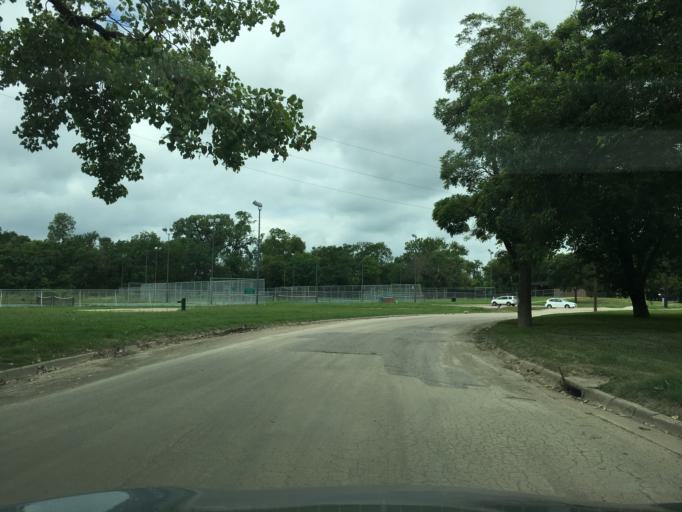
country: US
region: Texas
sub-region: Dallas County
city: University Park
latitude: 32.8761
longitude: -96.7430
